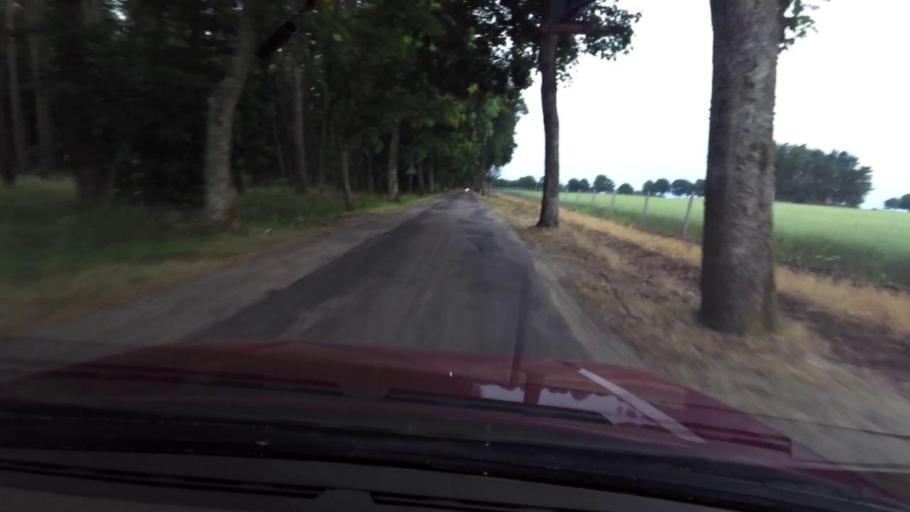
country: PL
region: Pomeranian Voivodeship
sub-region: Powiat slupski
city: Kepice
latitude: 54.2025
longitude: 16.8160
